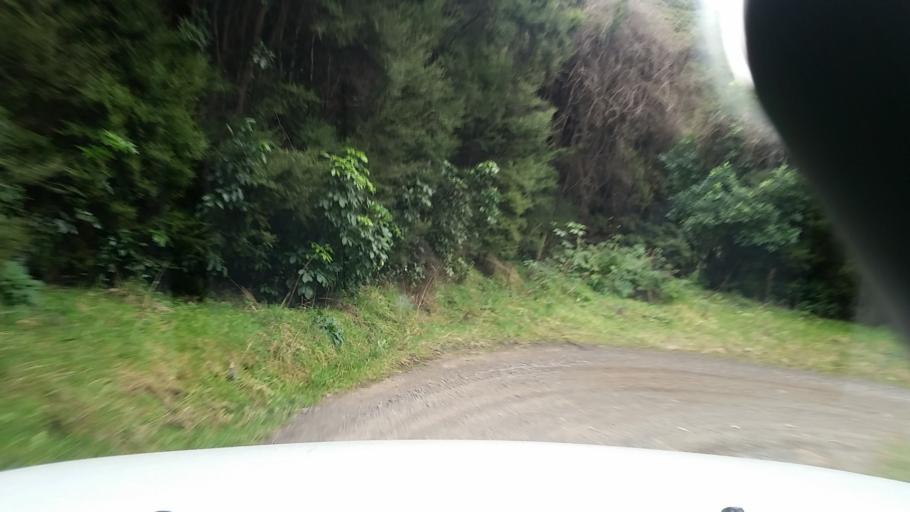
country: NZ
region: Canterbury
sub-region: Christchurch City
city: Christchurch
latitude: -43.7830
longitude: 172.8337
